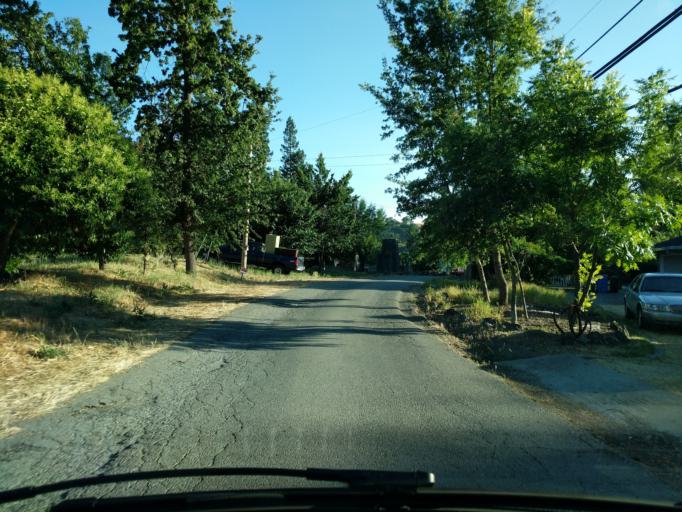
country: US
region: California
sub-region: Contra Costa County
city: Diablo
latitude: 37.8326
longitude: -121.9520
